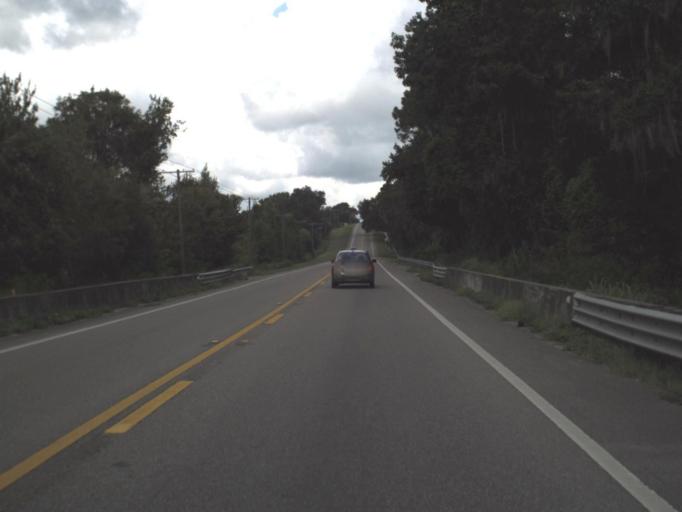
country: US
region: Florida
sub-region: Pasco County
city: Saint Leo
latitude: 28.3356
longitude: -82.2494
